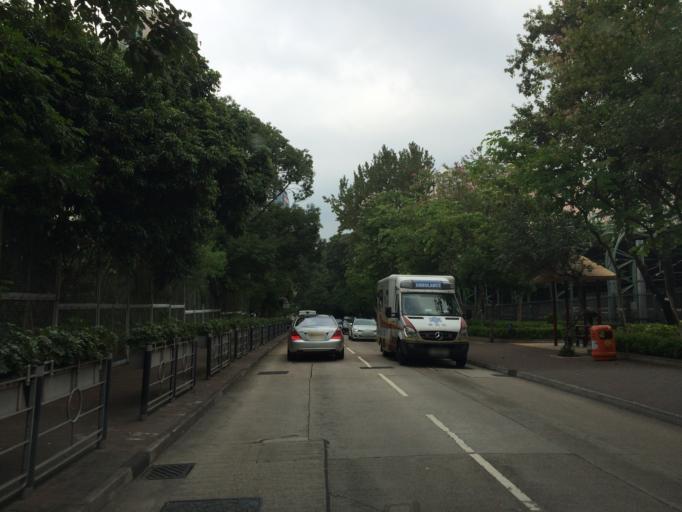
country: HK
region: Kowloon City
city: Kowloon
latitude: 22.3149
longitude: 114.1748
